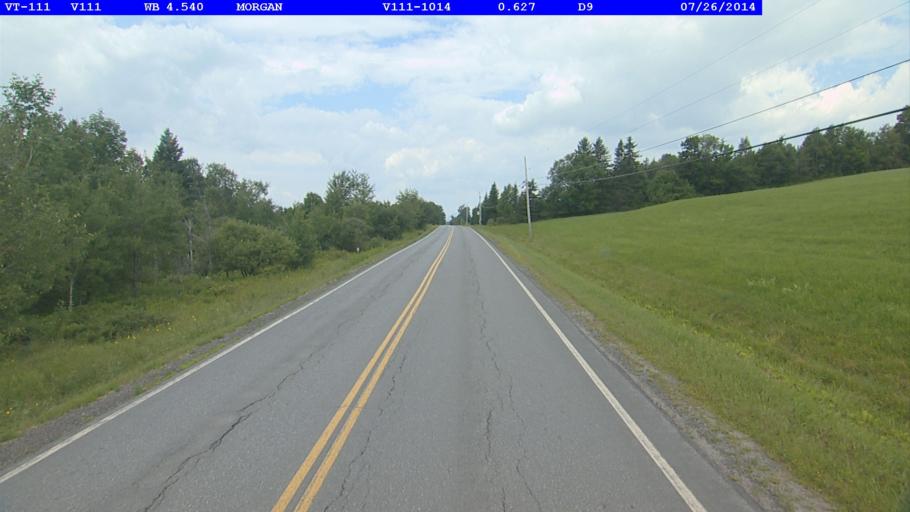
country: US
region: Vermont
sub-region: Orleans County
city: Newport
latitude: 44.9253
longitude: -72.0537
